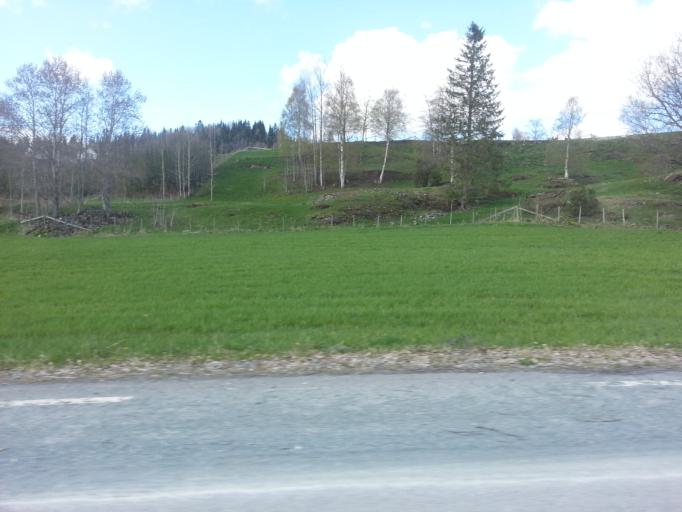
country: NO
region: Nord-Trondelag
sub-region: Levanger
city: Skogn
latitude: 63.6339
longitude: 11.2193
